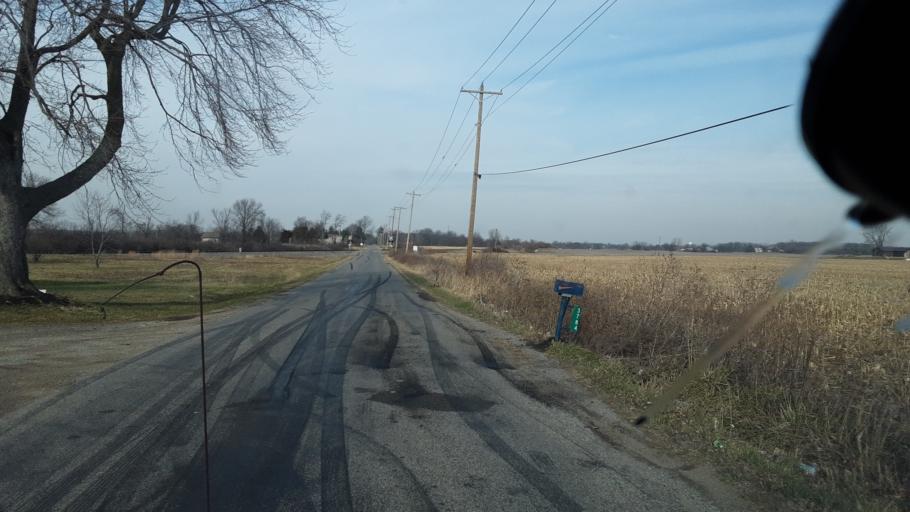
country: US
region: Indiana
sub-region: DeKalb County
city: Butler
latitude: 41.3967
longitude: -84.8891
